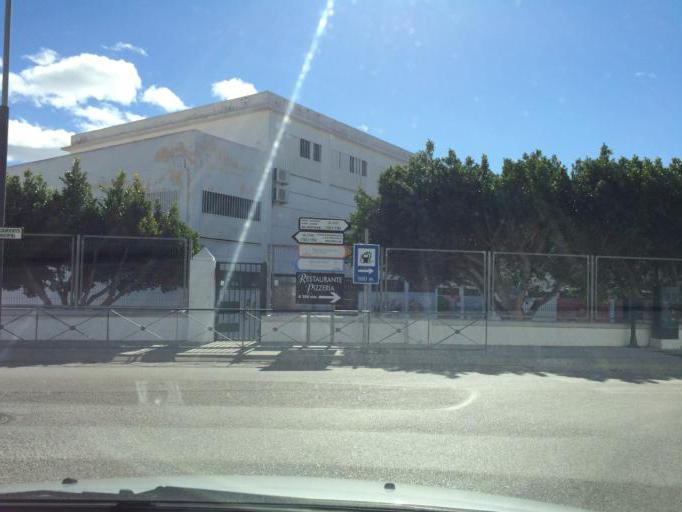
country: ES
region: Andalusia
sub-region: Provincia de Almeria
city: Nijar
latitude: 36.9597
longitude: -2.2053
